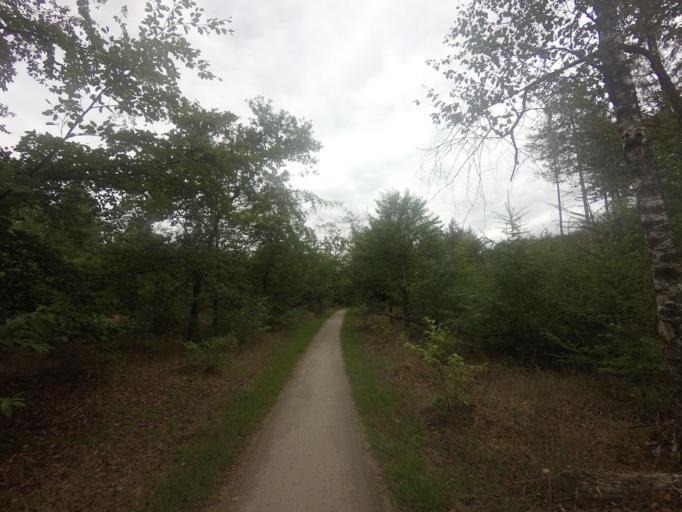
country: NL
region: Drenthe
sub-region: Gemeente Westerveld
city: Dwingeloo
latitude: 52.9308
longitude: 6.3168
